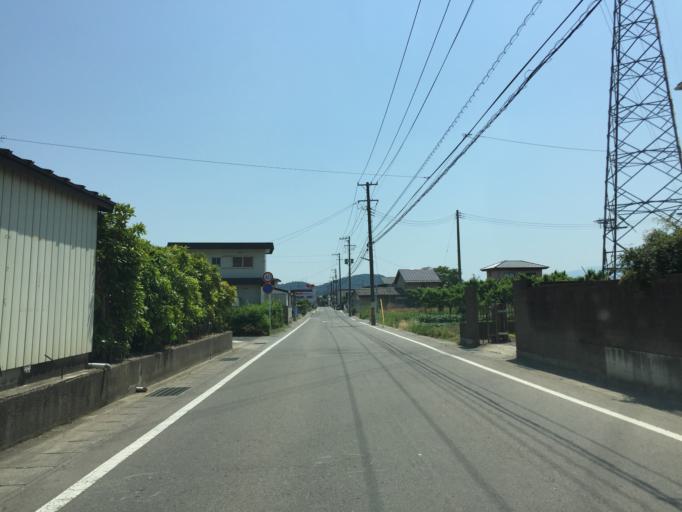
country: JP
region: Fukushima
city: Fukushima-shi
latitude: 37.8054
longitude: 140.4738
